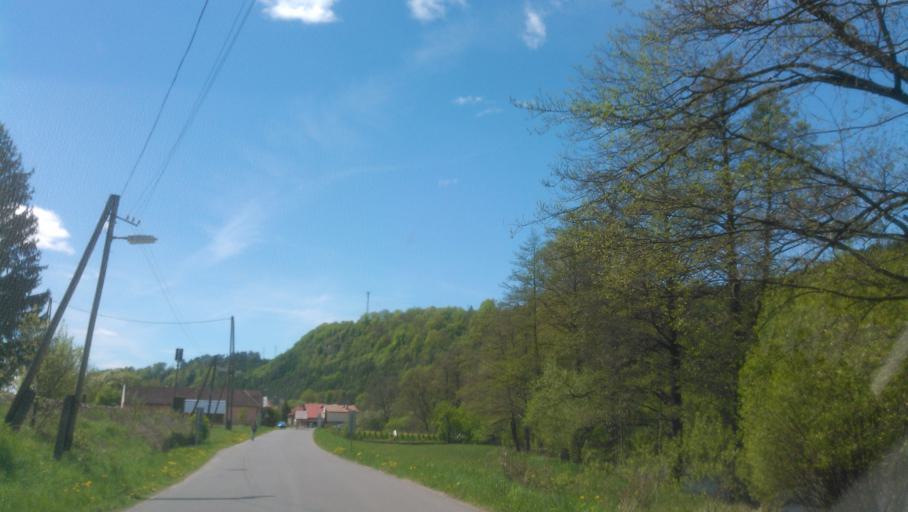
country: SK
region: Banskobystricky
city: Hrochot,Slovakia
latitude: 48.8146
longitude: 19.4216
